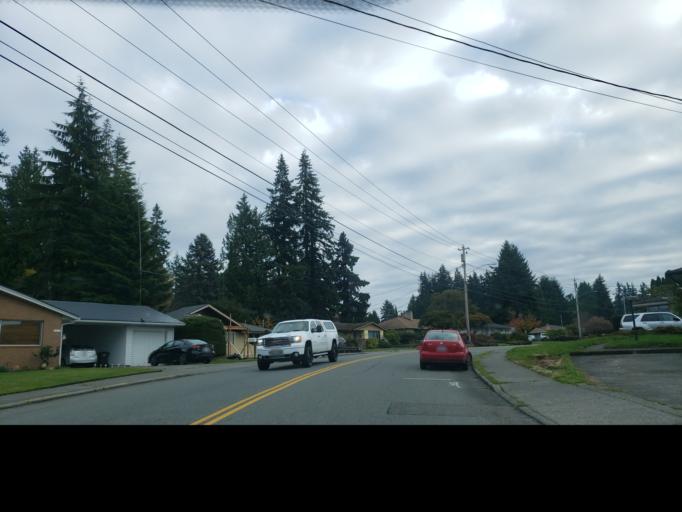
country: US
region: Washington
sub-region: Snohomish County
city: Everett
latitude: 47.9366
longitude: -122.2279
